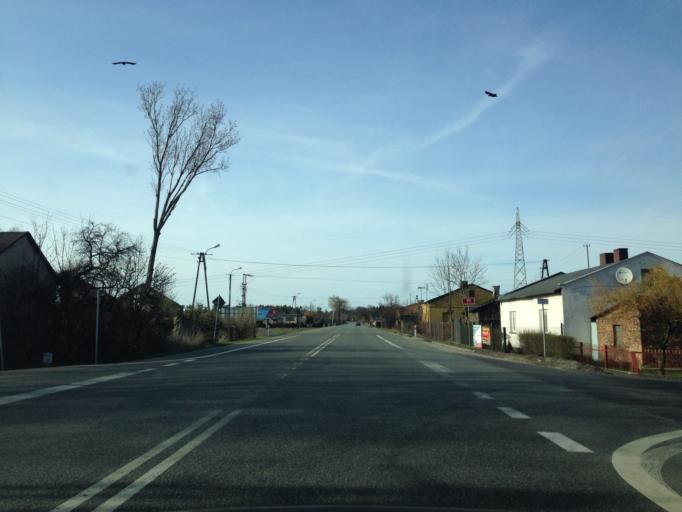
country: PL
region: Lodz Voivodeship
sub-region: Powiat kutnowski
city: Krosniewice
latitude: 52.2752
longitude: 19.1647
